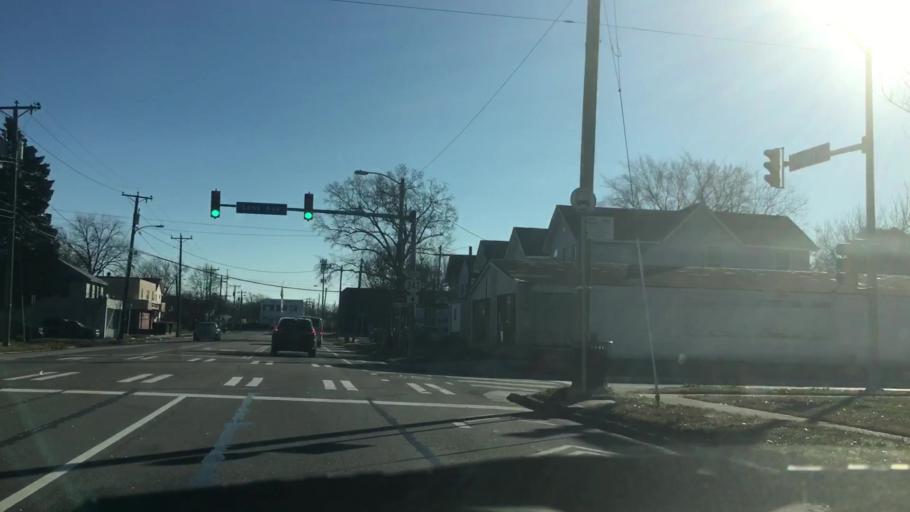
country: US
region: Virginia
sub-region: City of Norfolk
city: Norfolk
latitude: 36.8760
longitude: -76.2569
